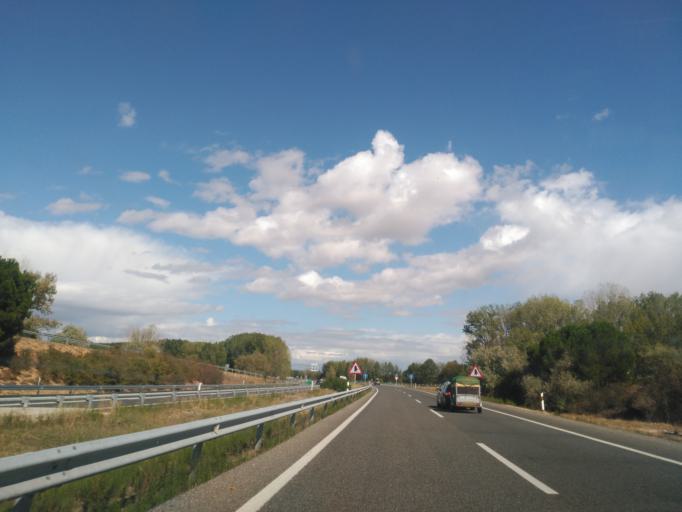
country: ES
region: Castille and Leon
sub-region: Provincia de Burgos
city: Celada del Camino
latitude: 42.2661
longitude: -3.9284
